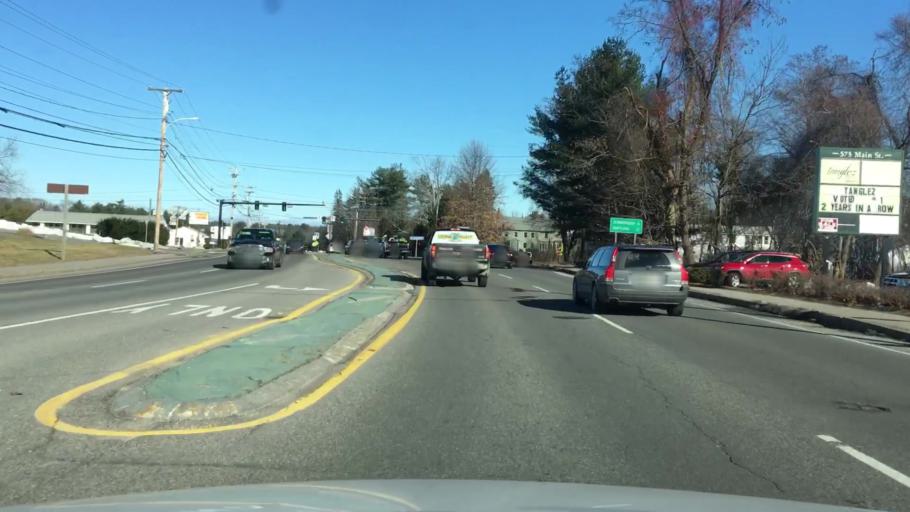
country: US
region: Maine
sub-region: York County
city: Saco
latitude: 43.5139
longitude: -70.4301
